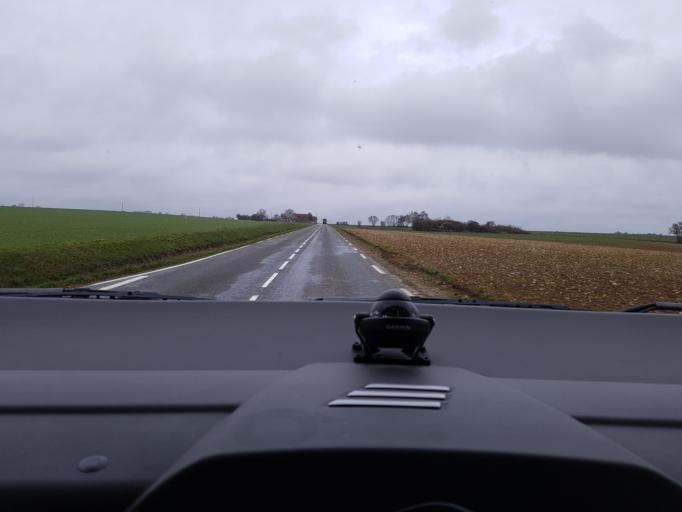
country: FR
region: Picardie
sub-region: Departement de l'Oise
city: Songeons
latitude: 49.5112
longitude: 1.8128
